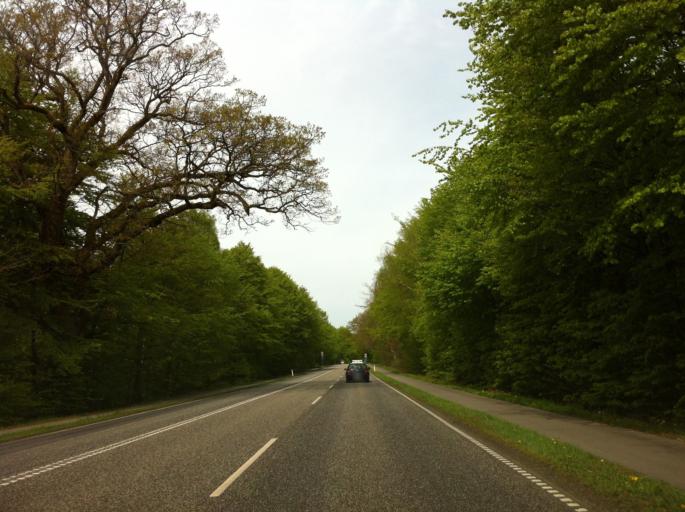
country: DK
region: Capital Region
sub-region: Allerod Kommune
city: Lillerod
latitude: 55.9011
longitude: 12.3602
